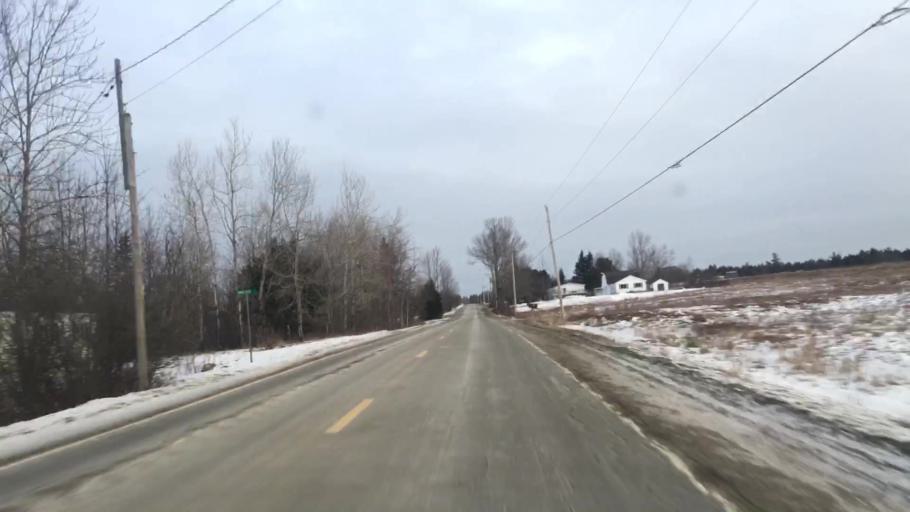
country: US
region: Maine
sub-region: Hancock County
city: Franklin
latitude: 44.7136
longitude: -68.3377
